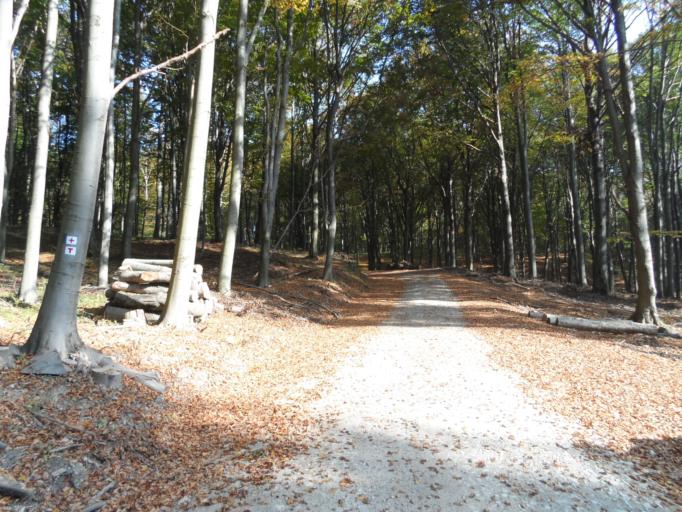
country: HU
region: Veszprem
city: Herend
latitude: 47.1918
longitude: 17.7585
